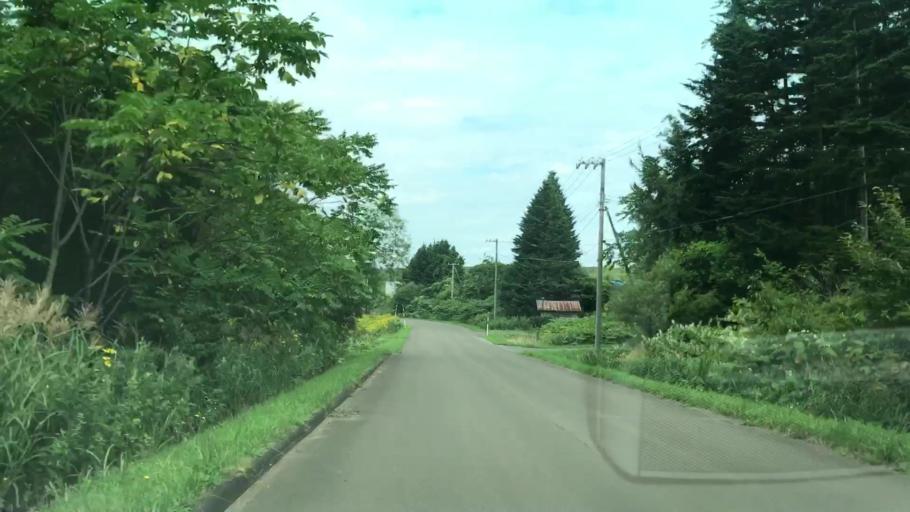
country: JP
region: Hokkaido
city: Yoichi
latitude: 43.1726
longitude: 140.8287
